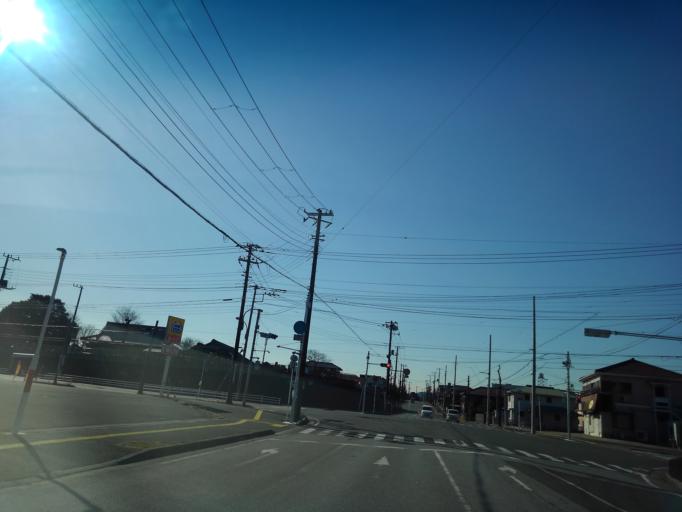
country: JP
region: Chiba
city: Kimitsu
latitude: 35.3323
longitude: 139.9165
